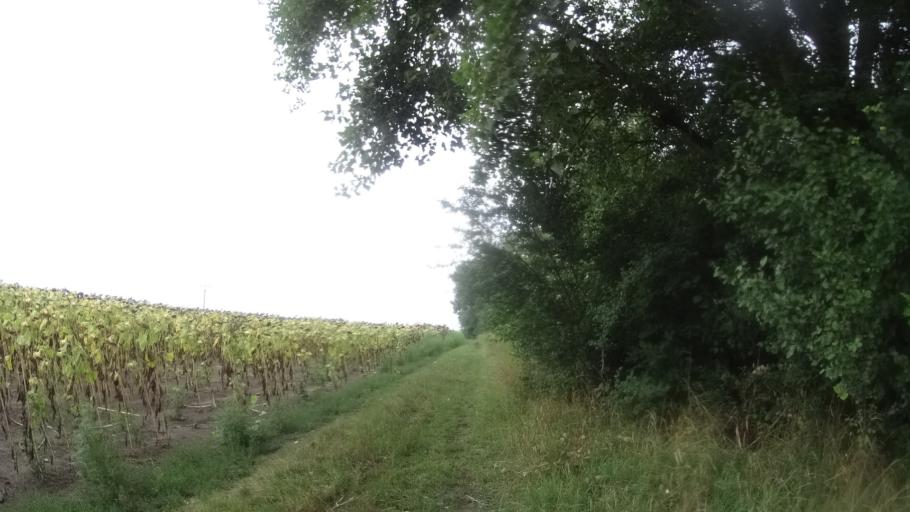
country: SK
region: Nitriansky
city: Komarno
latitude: 47.7612
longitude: 18.0871
